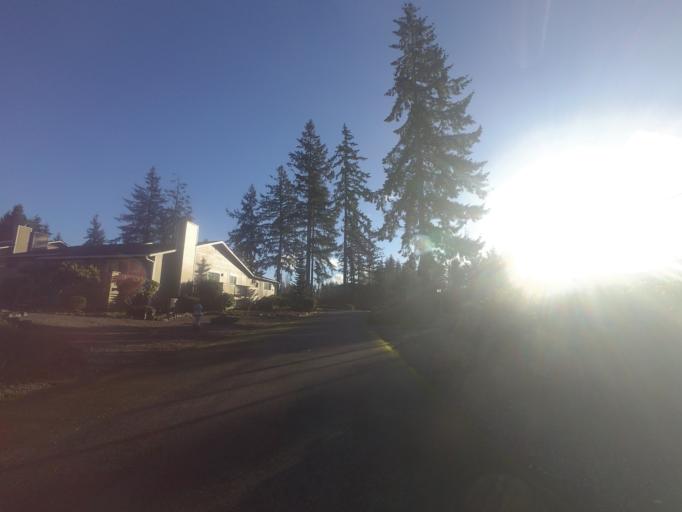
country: US
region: Washington
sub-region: Pierce County
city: University Place
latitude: 47.2221
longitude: -122.5339
